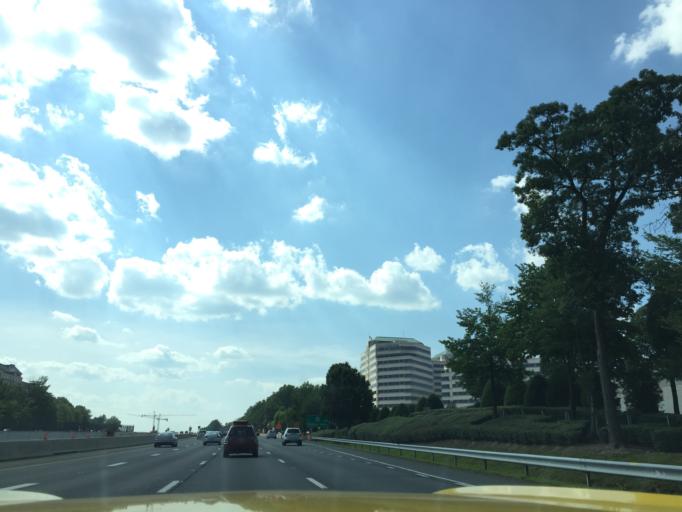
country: US
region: Virginia
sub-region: Fairfax County
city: Reston
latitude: 38.9504
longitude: -77.3470
